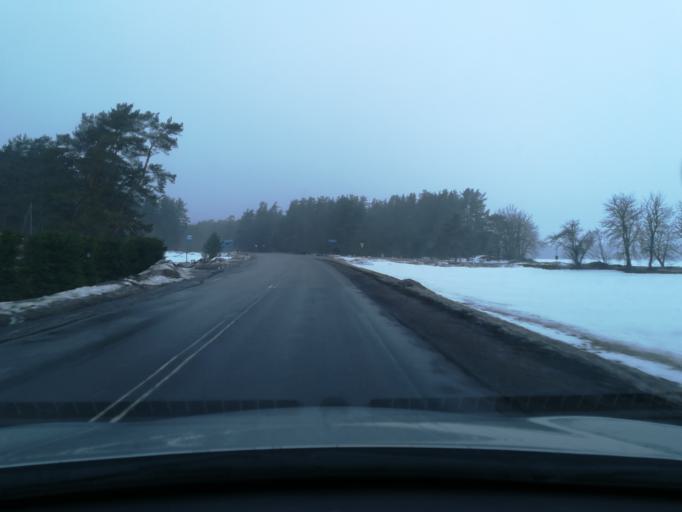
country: EE
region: Harju
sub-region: Raasiku vald
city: Arukula
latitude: 59.3554
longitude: 25.0769
